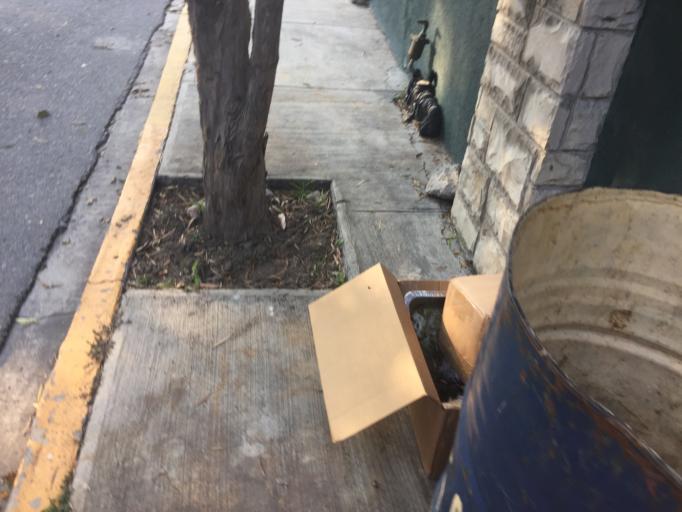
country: MX
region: Nuevo Leon
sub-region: San Pedro Garza Garcia
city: San Pedro Garza Garcia
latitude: 25.6572
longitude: -100.3986
